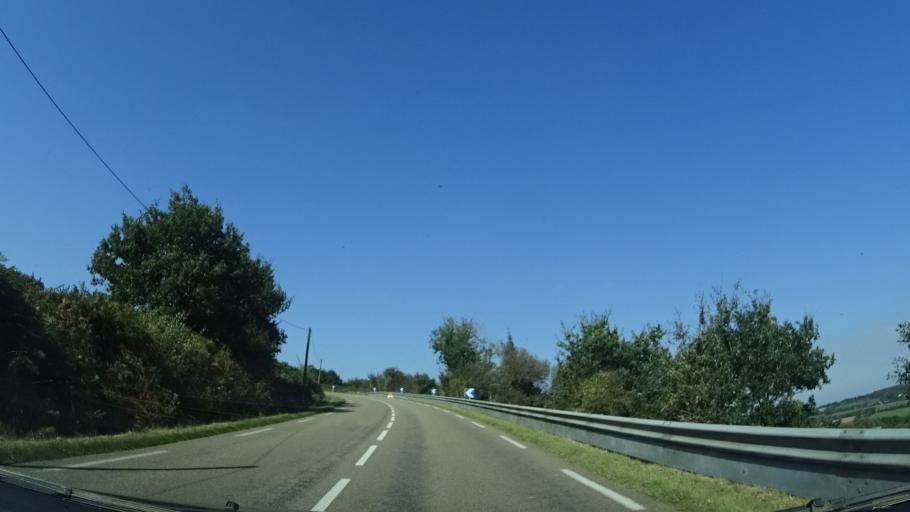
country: FR
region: Brittany
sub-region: Departement du Finistere
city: Cast
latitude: 48.1786
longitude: -4.1225
